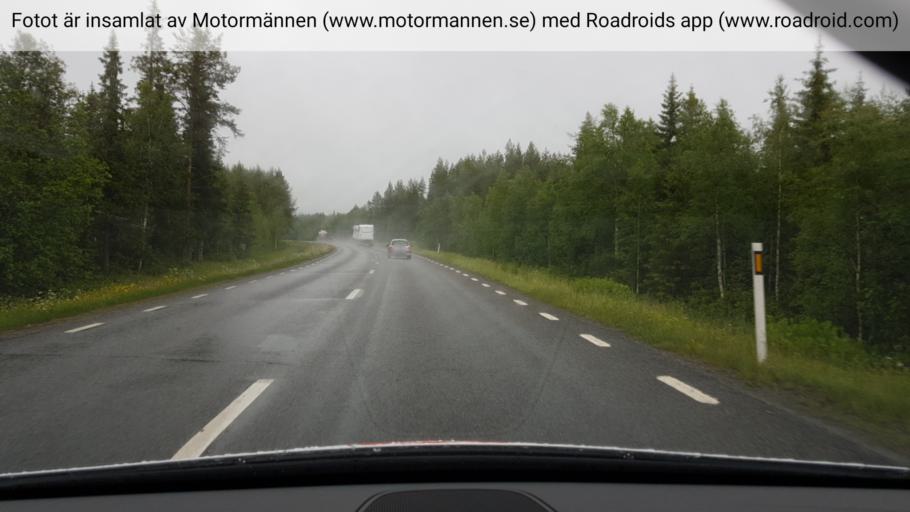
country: SE
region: Jaemtland
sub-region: OEstersunds Kommun
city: Lit
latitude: 63.4840
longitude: 15.2340
